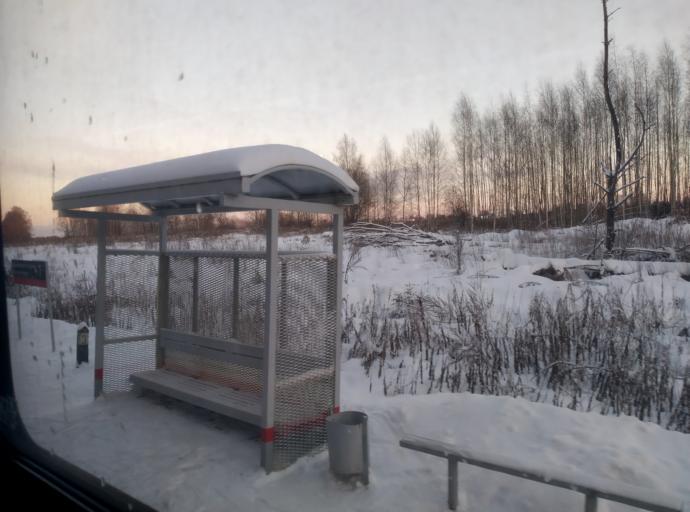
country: RU
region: Tverskaya
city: Ves'yegonsk
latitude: 58.5445
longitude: 37.0636
